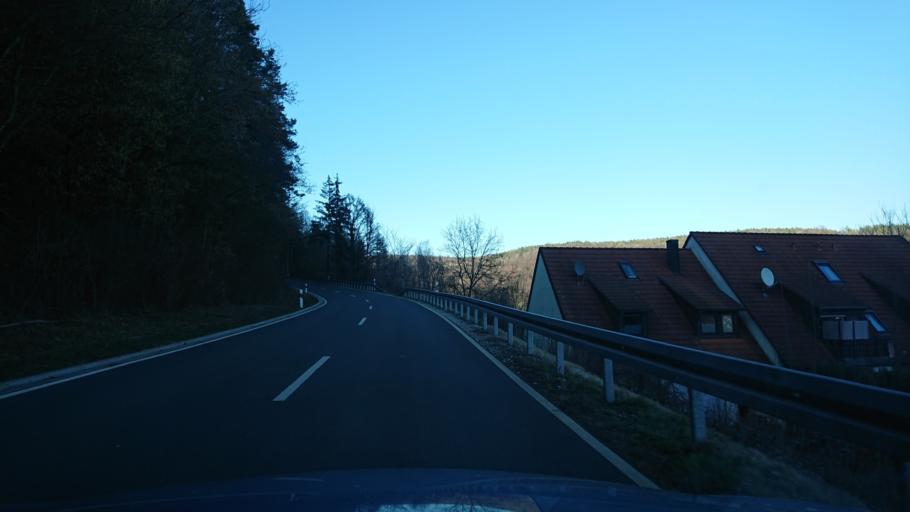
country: DE
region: Bavaria
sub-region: Upper Franconia
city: Ebermannstadt
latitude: 49.7856
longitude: 11.1736
